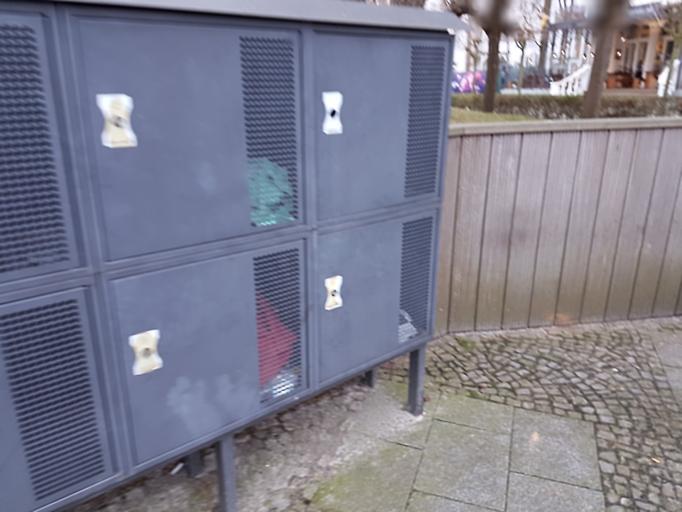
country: DE
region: Mecklenburg-Vorpommern
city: Ostseebad Binz
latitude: 54.4014
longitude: 13.6150
